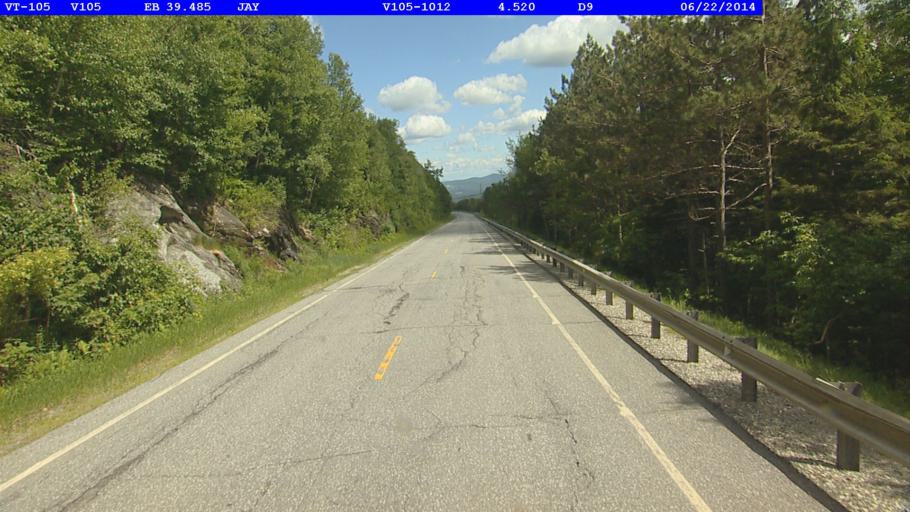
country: CA
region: Quebec
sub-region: Monteregie
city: Sutton
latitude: 44.9844
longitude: -72.4929
